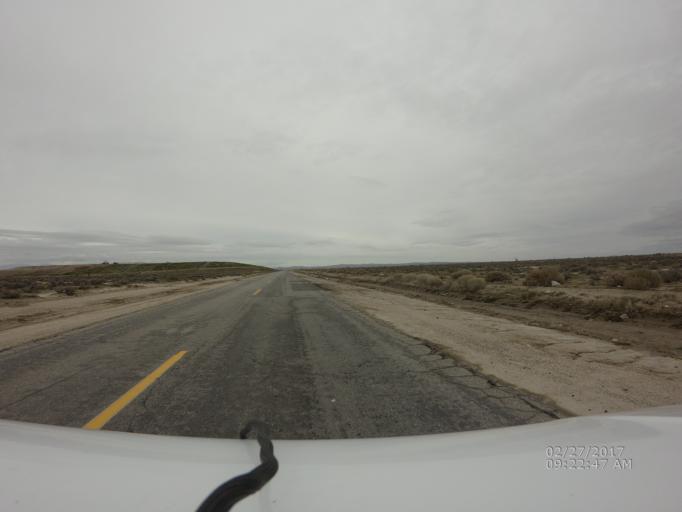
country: US
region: California
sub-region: Los Angeles County
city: Lancaster
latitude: 34.7376
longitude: -118.1130
